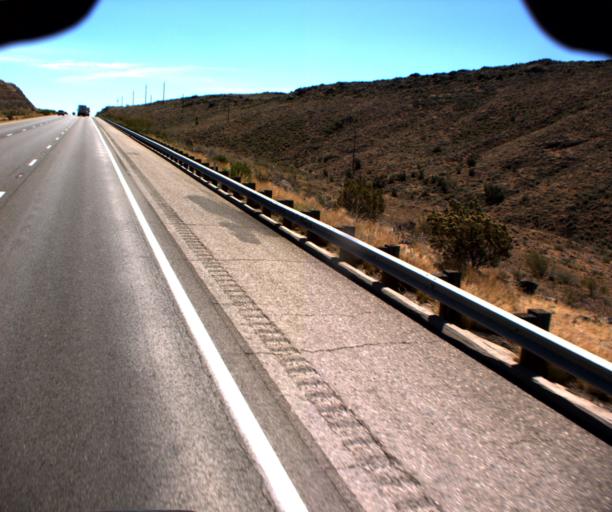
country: US
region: Arizona
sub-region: Mohave County
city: Kingman
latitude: 35.2113
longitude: -114.1098
